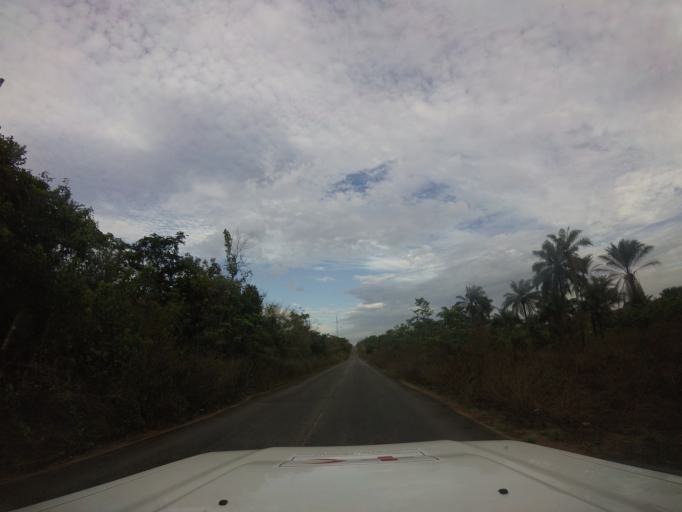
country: LR
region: Bomi
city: Tubmanburg
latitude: 6.6937
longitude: -10.8959
